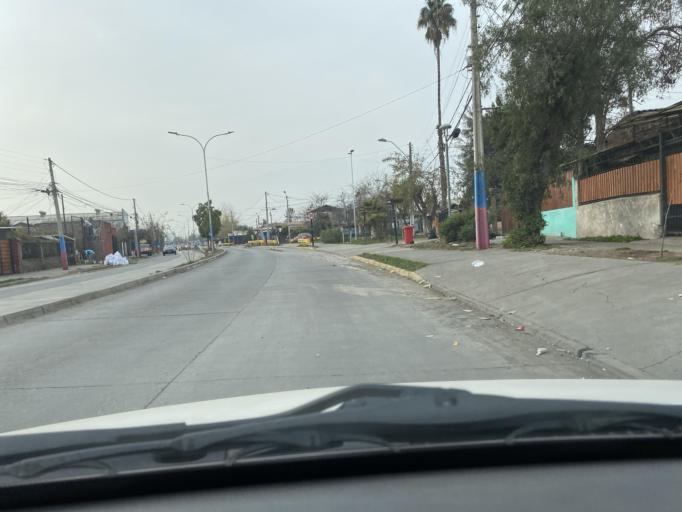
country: CL
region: Santiago Metropolitan
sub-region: Provincia de Santiago
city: Santiago
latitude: -33.5179
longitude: -70.6274
